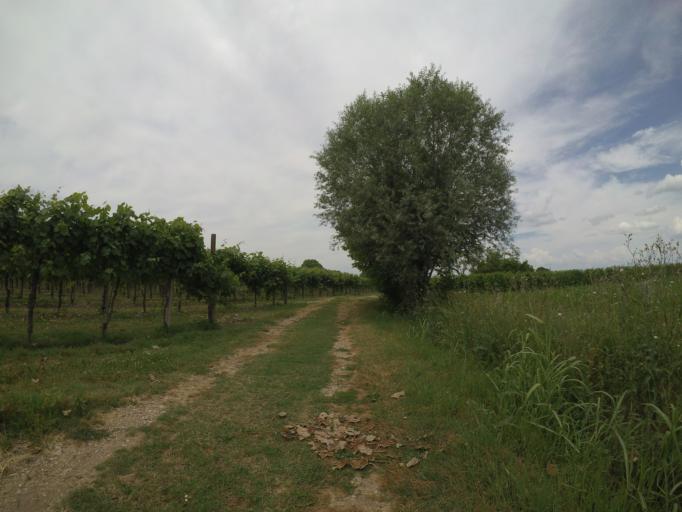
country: IT
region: Friuli Venezia Giulia
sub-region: Provincia di Udine
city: Bertiolo
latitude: 45.9323
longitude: 13.0591
